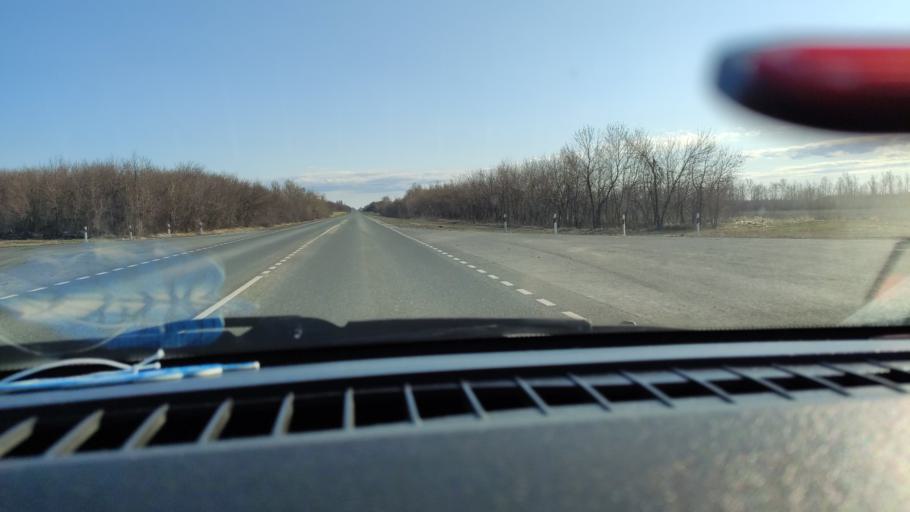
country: RU
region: Saratov
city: Khvalynsk
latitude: 52.5893
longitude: 48.1284
